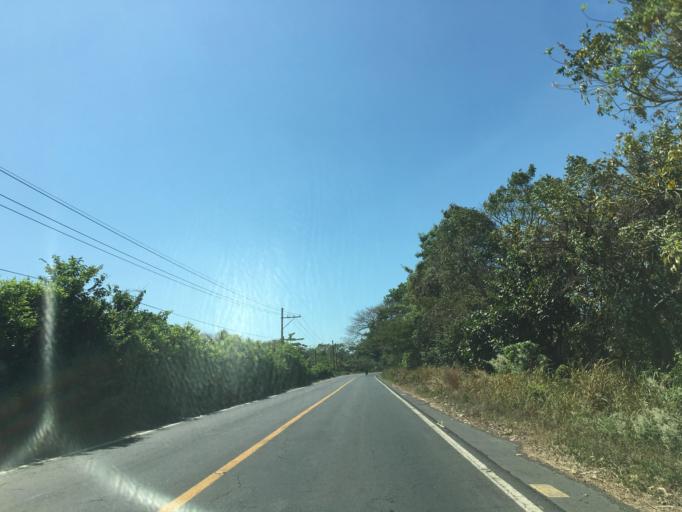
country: GT
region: Escuintla
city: Puerto San Jose
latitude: 14.0069
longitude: -90.8938
